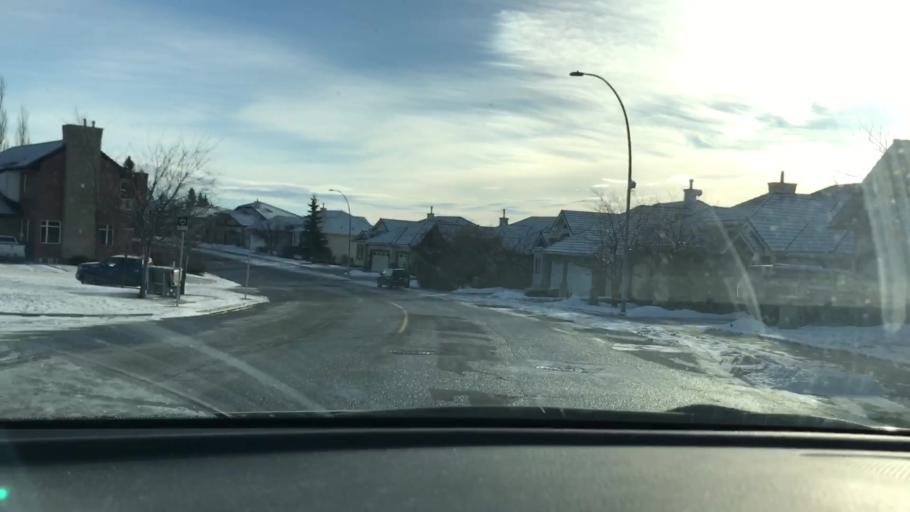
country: CA
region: Alberta
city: Calgary
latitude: 51.0230
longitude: -114.1772
